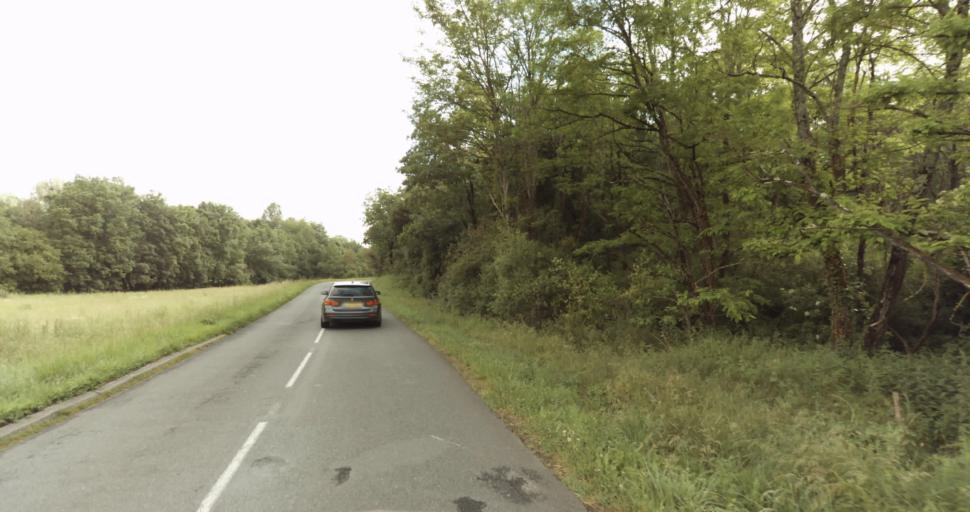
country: FR
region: Aquitaine
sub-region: Departement de la Dordogne
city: Mouleydier
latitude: 44.9091
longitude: 0.6637
